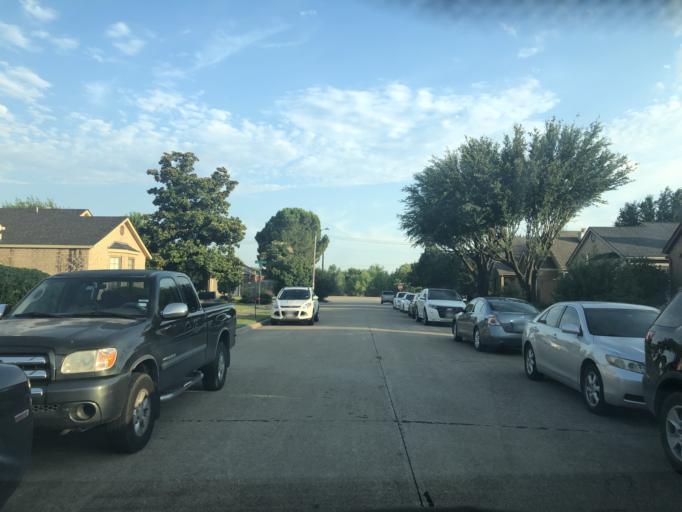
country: US
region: Texas
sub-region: Dallas County
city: Irving
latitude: 32.7840
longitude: -96.9615
